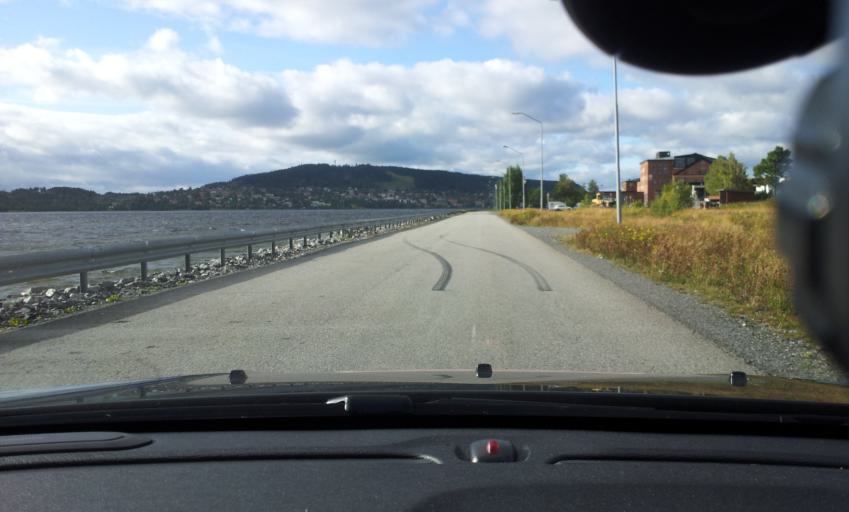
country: SE
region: Jaemtland
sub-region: OEstersunds Kommun
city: Ostersund
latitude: 63.1631
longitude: 14.6442
